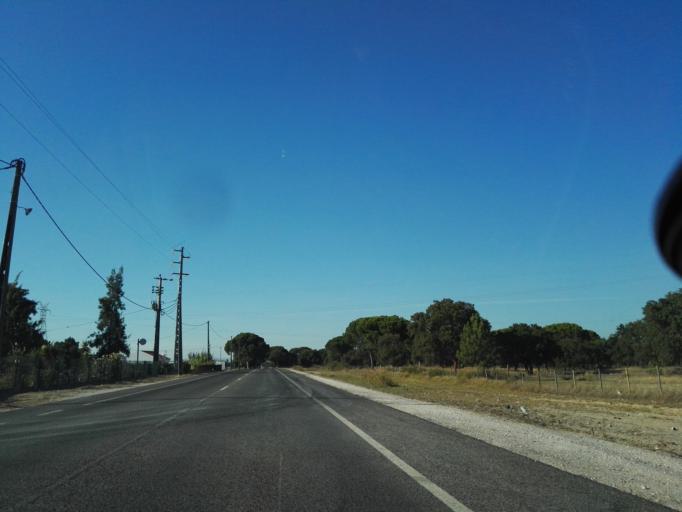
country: PT
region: Santarem
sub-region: Benavente
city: Samora Correia
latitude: 38.9011
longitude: -8.8411
